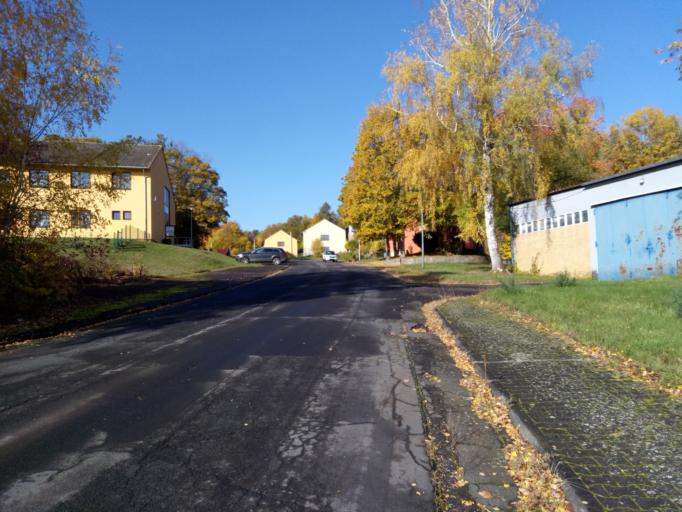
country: DE
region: Rheinland-Pfalz
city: Nussbaum
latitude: 49.8083
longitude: 7.6367
